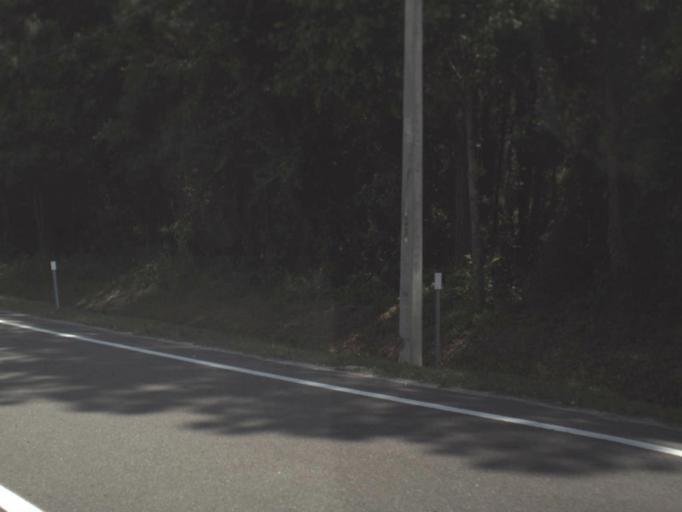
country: US
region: Florida
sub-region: Duval County
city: Jacksonville
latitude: 30.3587
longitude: -81.7126
